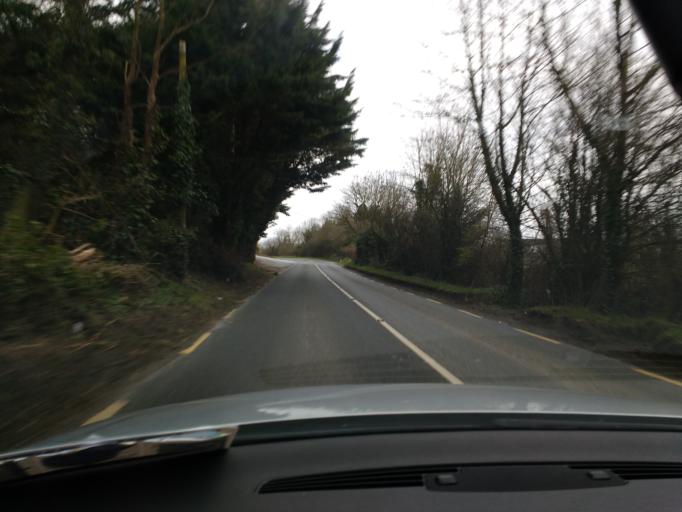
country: IE
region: Leinster
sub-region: Kilkenny
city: Kilkenny
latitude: 52.6893
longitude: -7.2761
